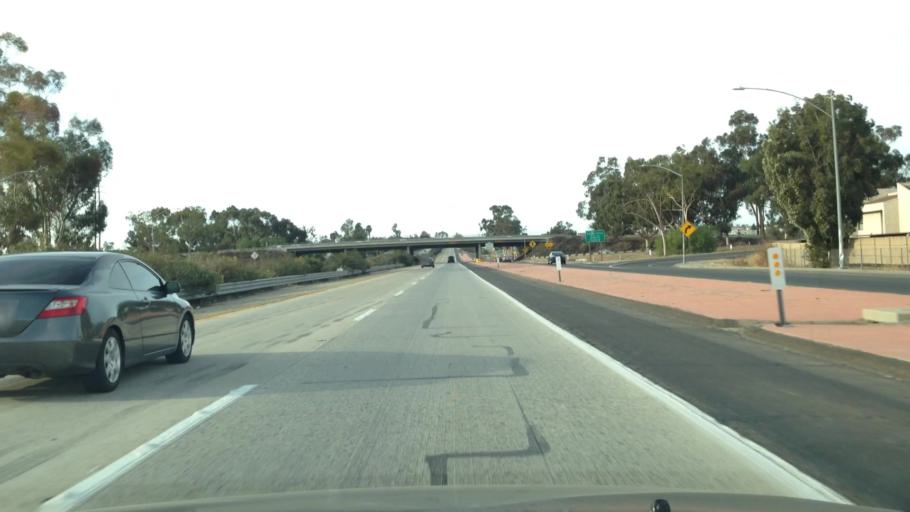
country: US
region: California
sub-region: Ventura County
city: Saticoy
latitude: 34.2913
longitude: -119.1538
